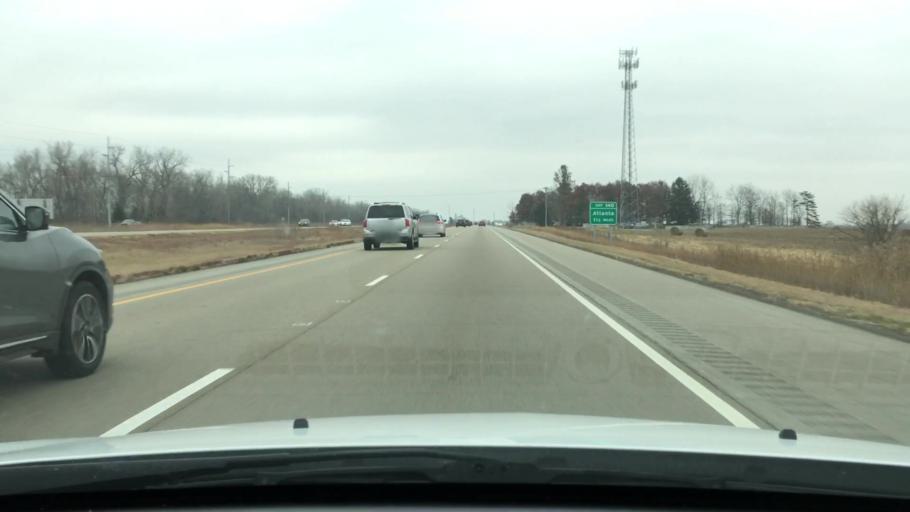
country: US
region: Illinois
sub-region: Logan County
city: Atlanta
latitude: 40.2433
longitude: -89.2512
